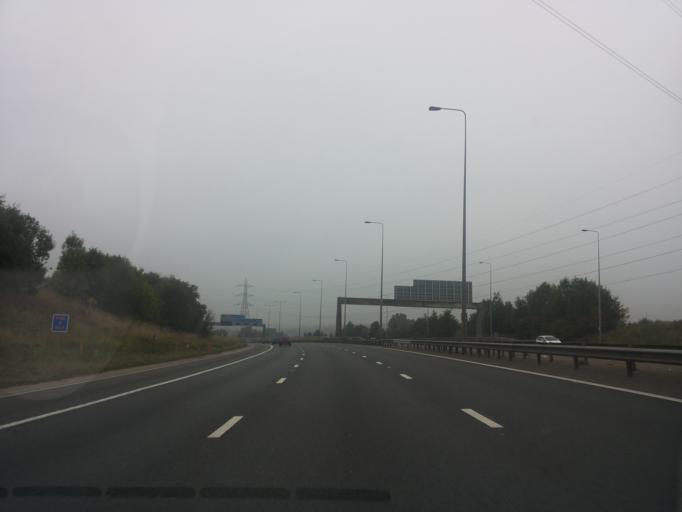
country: GB
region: England
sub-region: Borough of Rochdale
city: Middleton
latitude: 53.5401
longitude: -2.2149
